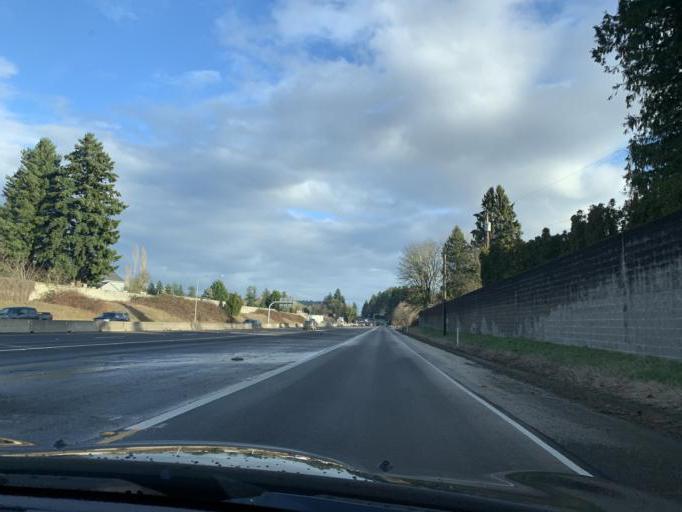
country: US
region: Washington
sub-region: Clark County
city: Mill Plain
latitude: 45.5904
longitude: -122.4998
